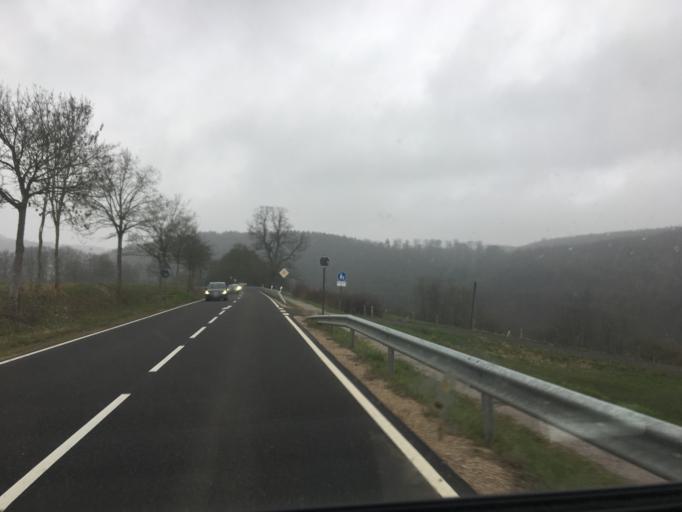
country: DE
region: North Rhine-Westphalia
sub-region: Regierungsbezirk Koln
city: Kall
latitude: 50.5053
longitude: 6.5691
